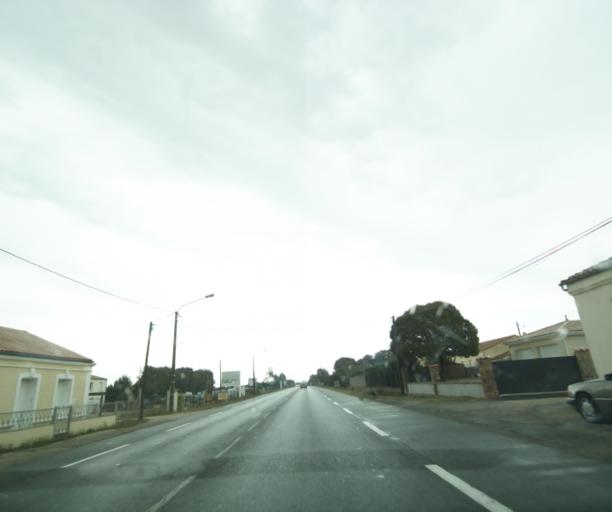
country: FR
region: Poitou-Charentes
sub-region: Departement de la Charente-Maritime
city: Tonnay-Charente
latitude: 45.9487
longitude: -0.9054
